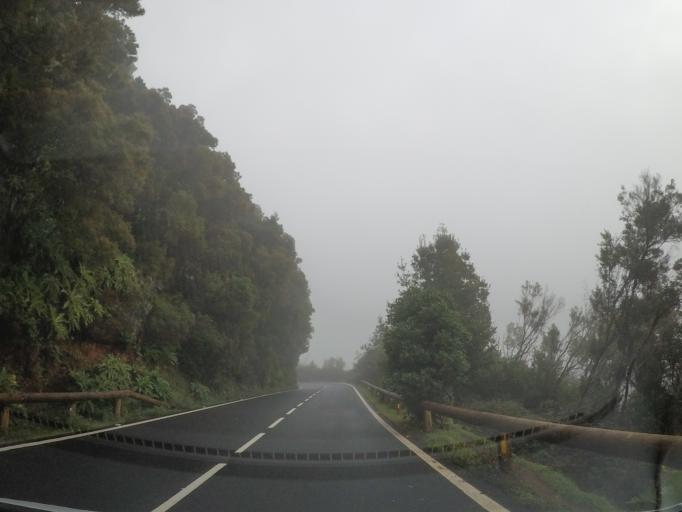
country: ES
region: Canary Islands
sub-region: Provincia de Santa Cruz de Tenerife
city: Alajero
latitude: 28.1173
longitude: -17.2462
